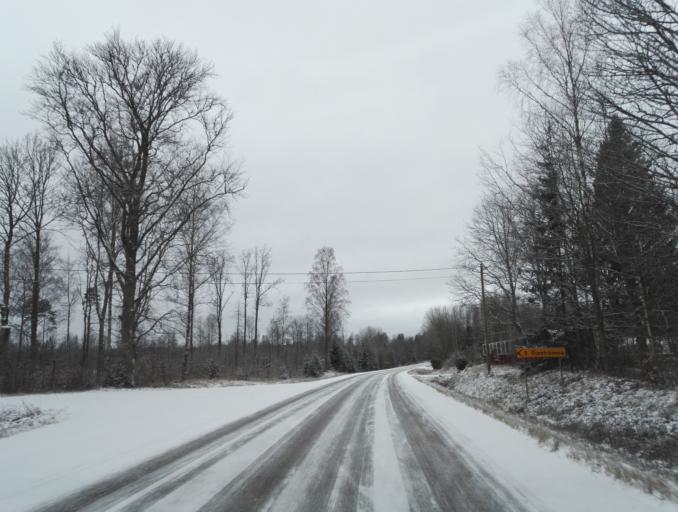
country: SE
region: Kronoberg
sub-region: Lessebo Kommun
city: Lessebo
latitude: 56.7296
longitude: 15.2200
